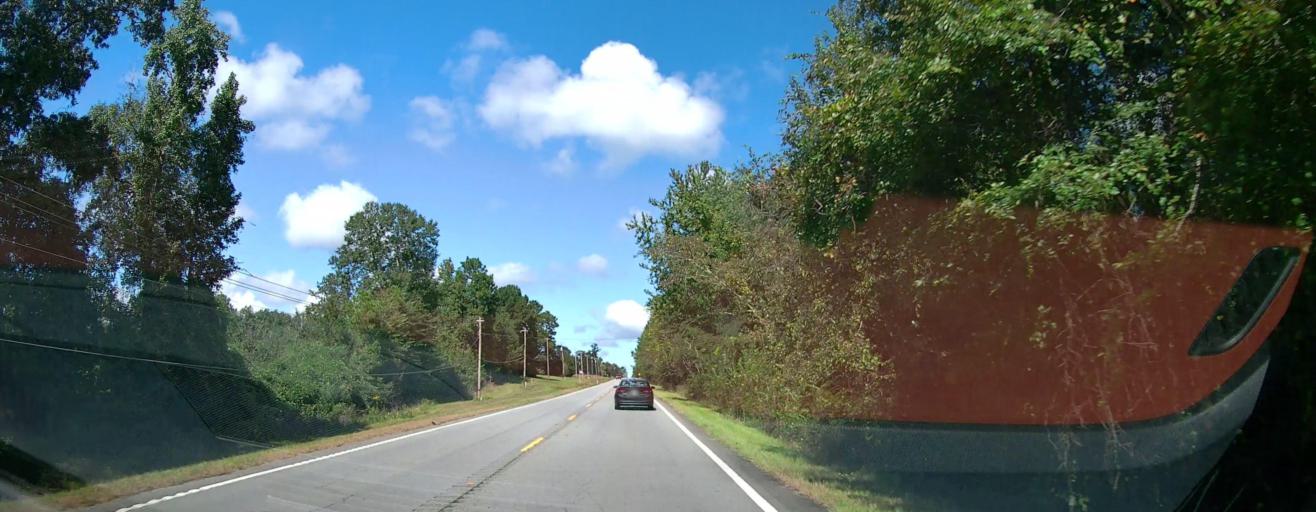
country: US
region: Georgia
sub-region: Bibb County
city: Macon
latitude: 32.8266
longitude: -83.5725
